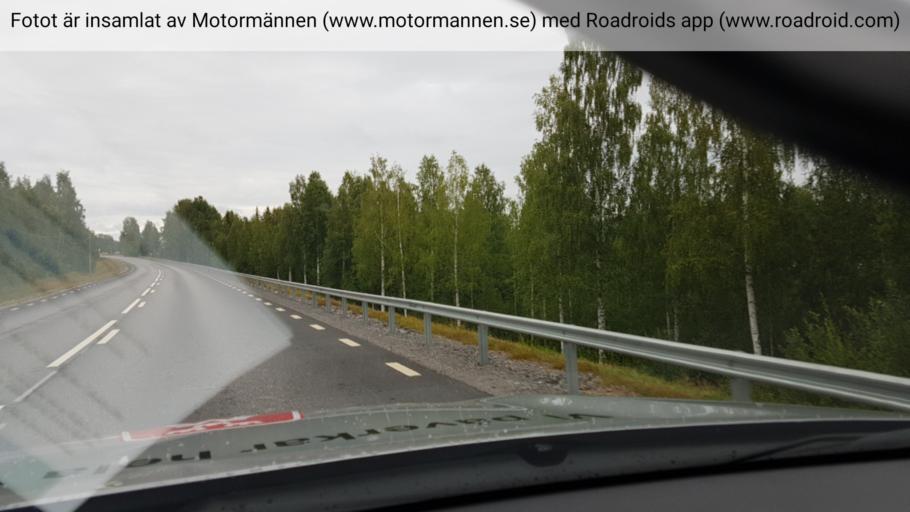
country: SE
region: Norrbotten
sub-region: Alvsbyns Kommun
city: AElvsbyn
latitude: 66.2771
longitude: 20.8234
